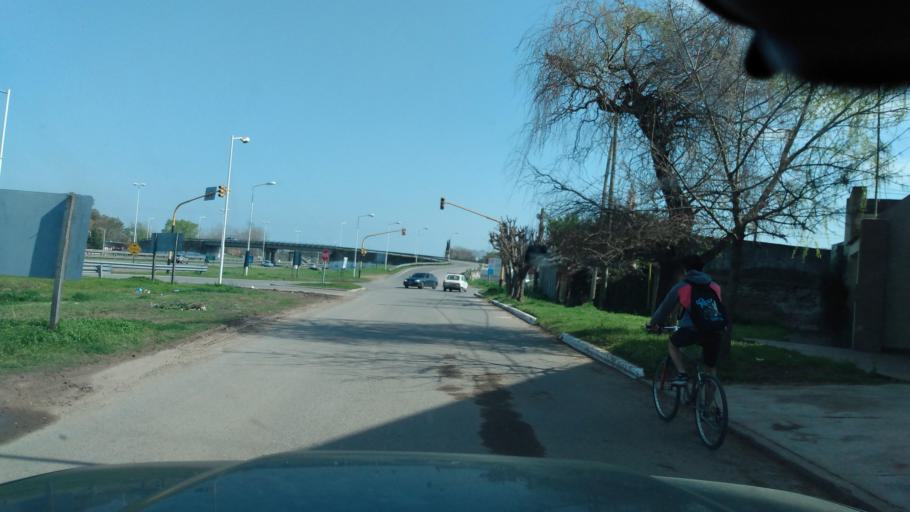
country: AR
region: Buenos Aires
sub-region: Partido de Lujan
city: Lujan
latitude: -34.5528
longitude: -59.1059
